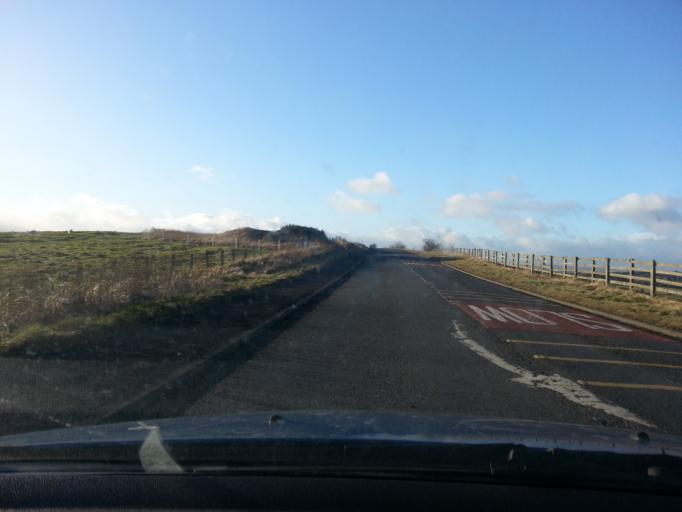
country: GB
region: England
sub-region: County Durham
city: Tow Law
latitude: 54.7412
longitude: -1.7892
